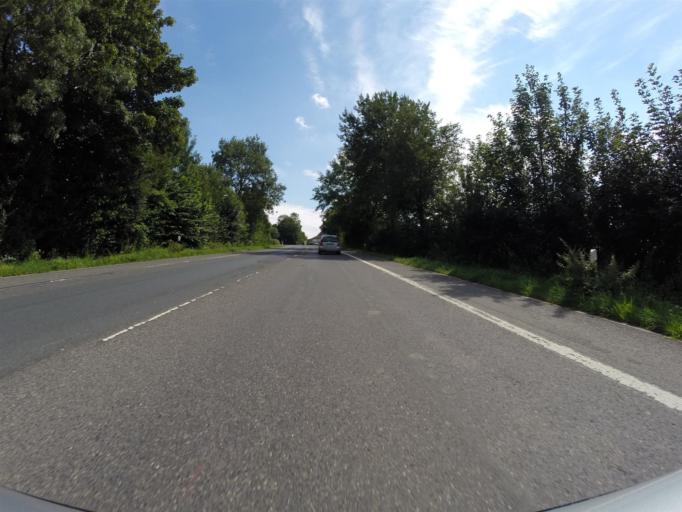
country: DE
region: North Rhine-Westphalia
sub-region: Regierungsbezirk Detmold
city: Rodinghausen
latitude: 52.2365
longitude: 8.5356
